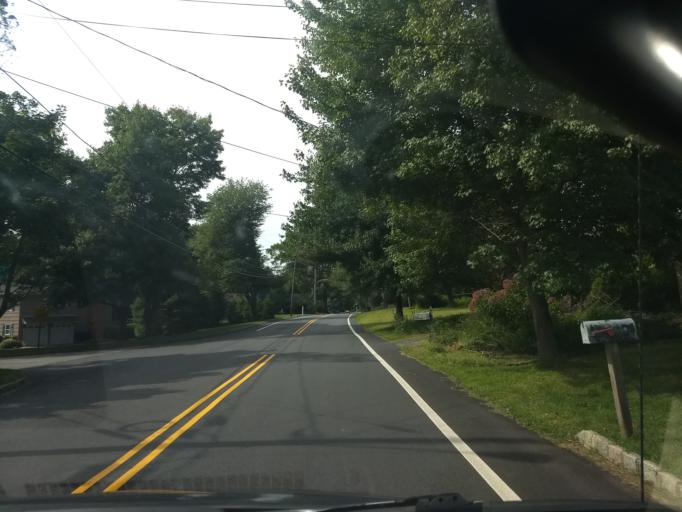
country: US
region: New Jersey
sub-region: Morris County
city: Morris Plains
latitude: 40.8166
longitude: -74.4953
